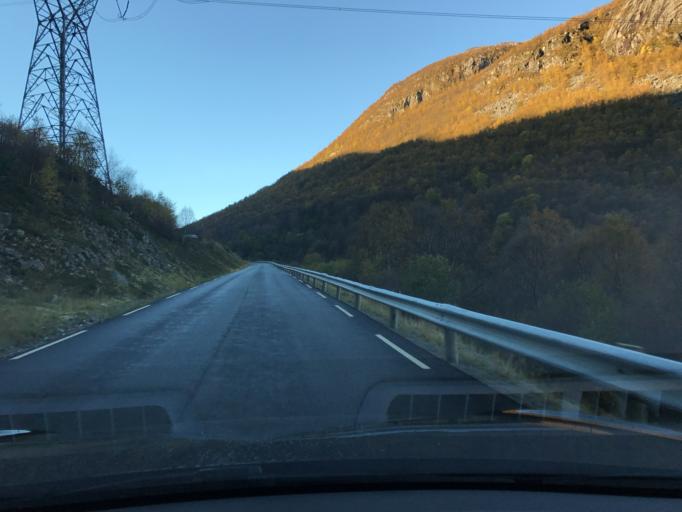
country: NO
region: Sogn og Fjordane
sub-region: Aurland
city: Aurlandsvangen
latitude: 60.8513
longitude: 7.3137
